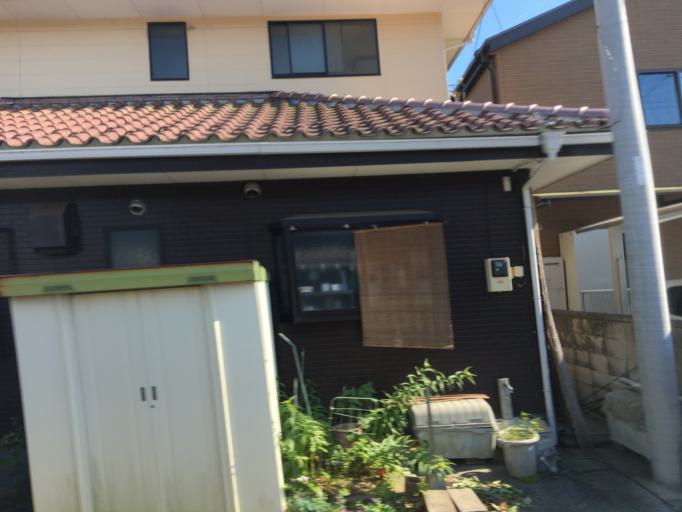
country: JP
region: Saitama
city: Sakado
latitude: 35.9640
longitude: 139.3569
